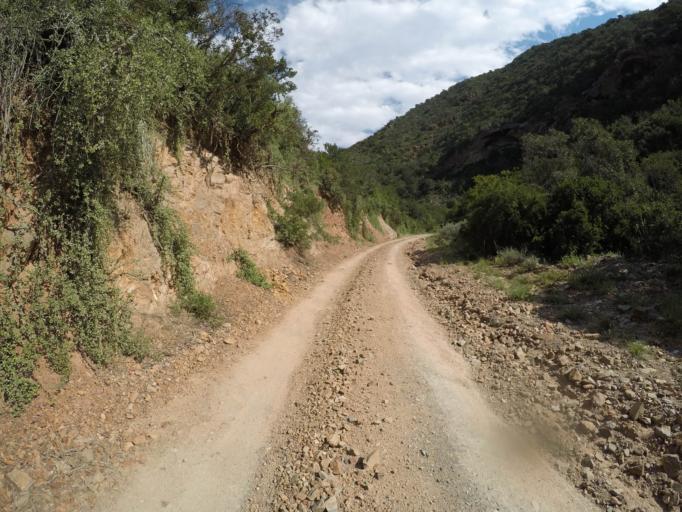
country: ZA
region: Eastern Cape
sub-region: Cacadu District Municipality
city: Kareedouw
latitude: -33.6538
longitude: 24.3486
